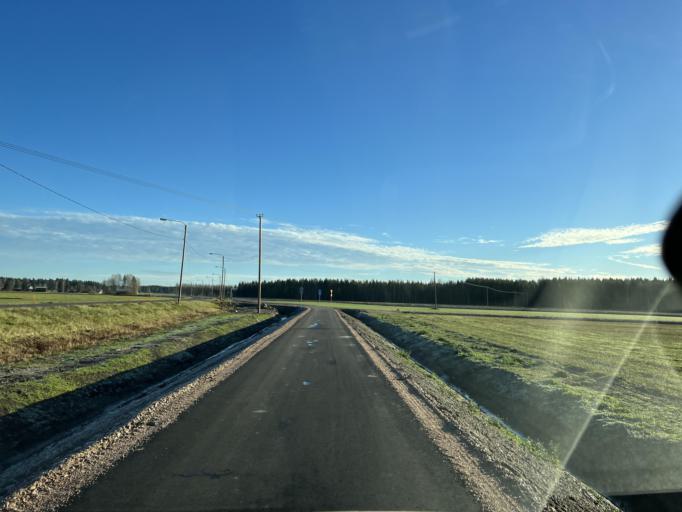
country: FI
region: Northern Ostrobothnia
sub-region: Nivala-Haapajaervi
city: Nivala
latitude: 63.9514
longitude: 24.8785
